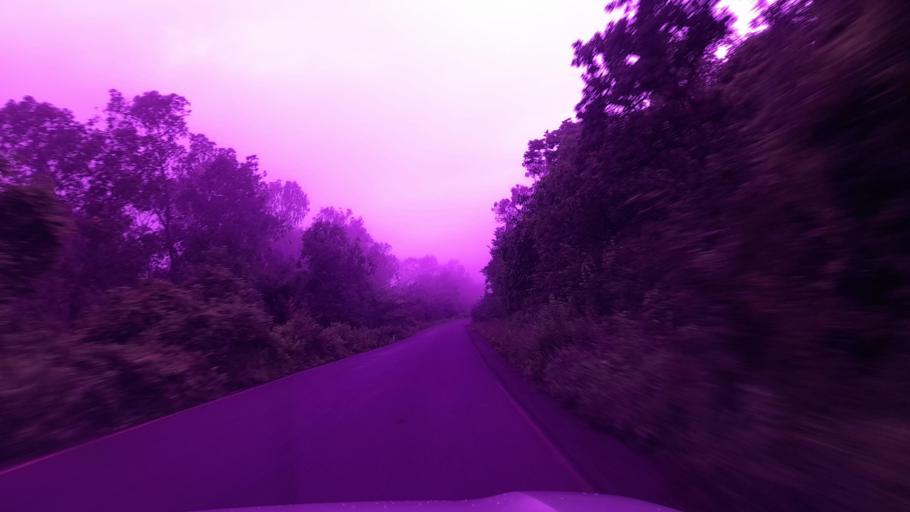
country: ET
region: Oromiya
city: Waliso
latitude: 8.1712
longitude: 37.5518
